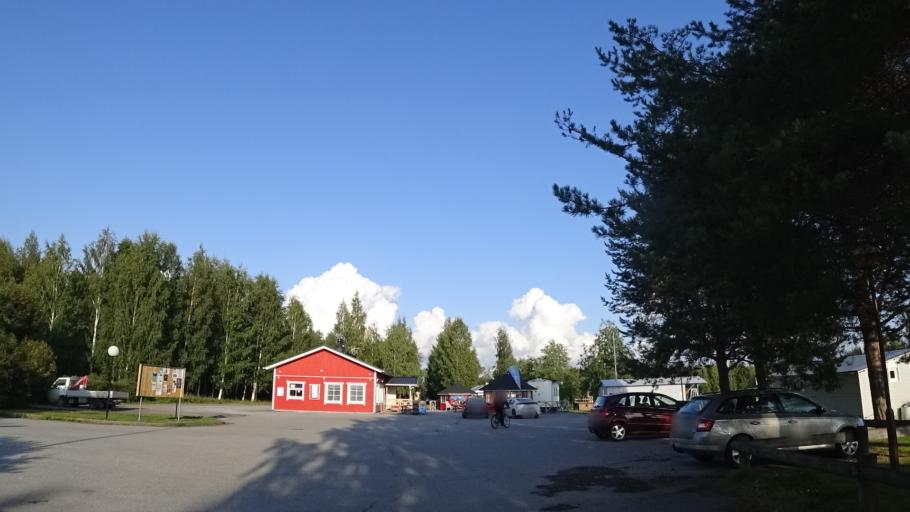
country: FI
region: North Karelia
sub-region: Pielisen Karjala
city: Lieksa
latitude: 63.3086
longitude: 30.0124
